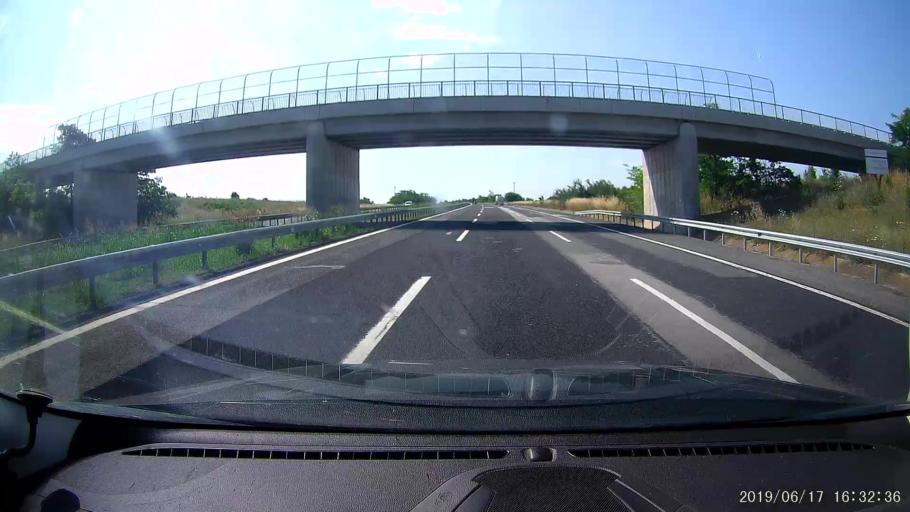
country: TR
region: Kirklareli
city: Buyukkaristiran
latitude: 41.3712
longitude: 27.5959
